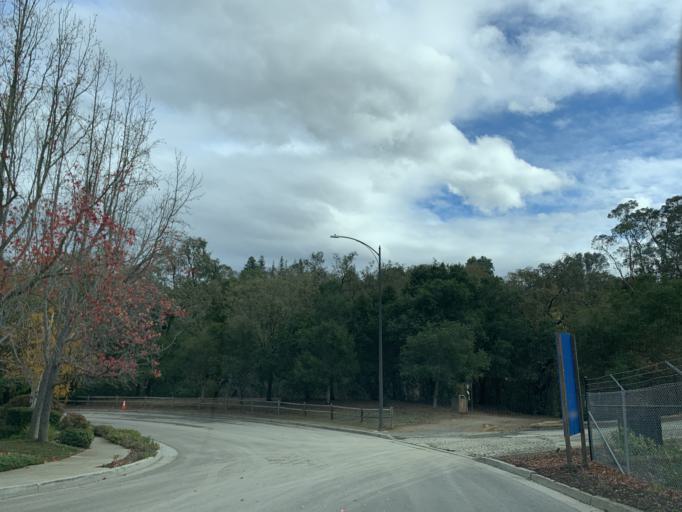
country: US
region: California
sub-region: Santa Clara County
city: Monte Sereno
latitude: 37.2571
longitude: -121.9811
